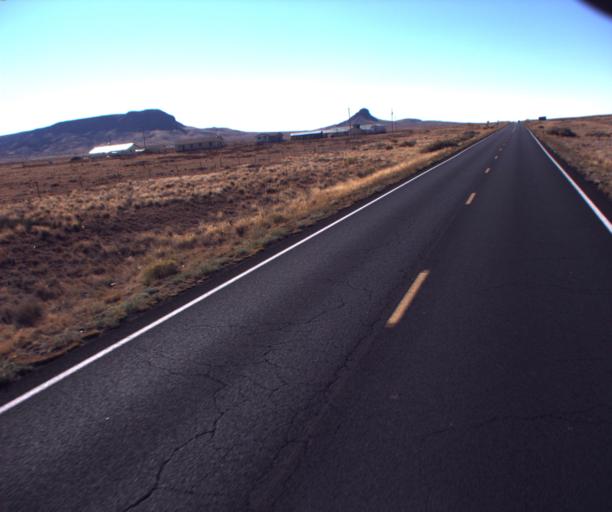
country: US
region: Arizona
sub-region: Navajo County
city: Dilkon
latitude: 35.4515
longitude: -110.4234
